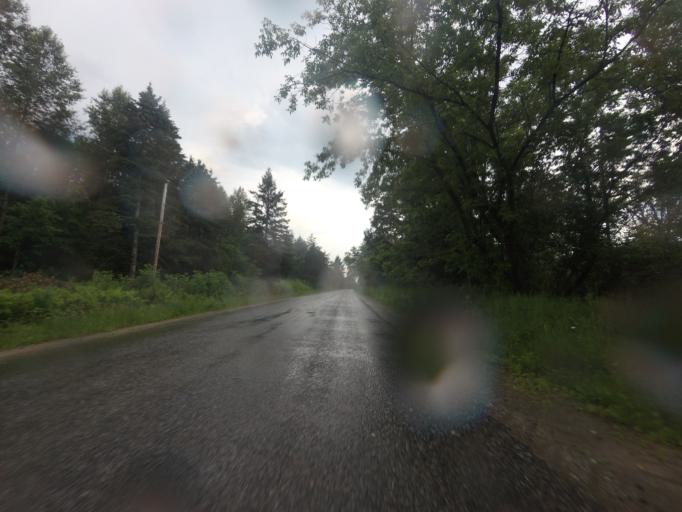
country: CA
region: Quebec
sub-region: Outaouais
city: Maniwaki
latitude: 46.4079
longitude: -75.9589
